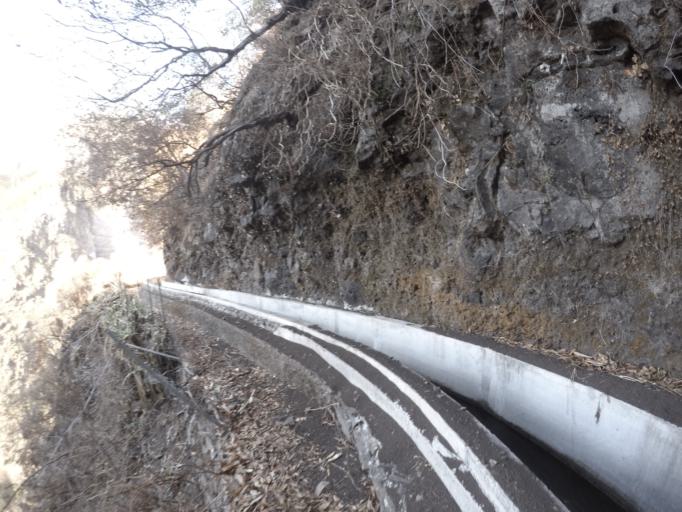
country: PT
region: Madeira
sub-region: Funchal
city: Nossa Senhora do Monte
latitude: 32.6883
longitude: -16.9146
